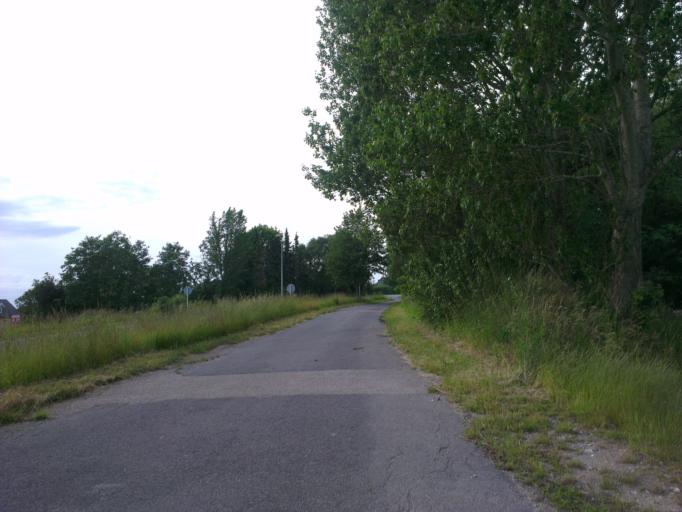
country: DK
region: Capital Region
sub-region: Frederikssund Kommune
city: Jaegerspris
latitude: 55.8122
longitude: 11.9826
